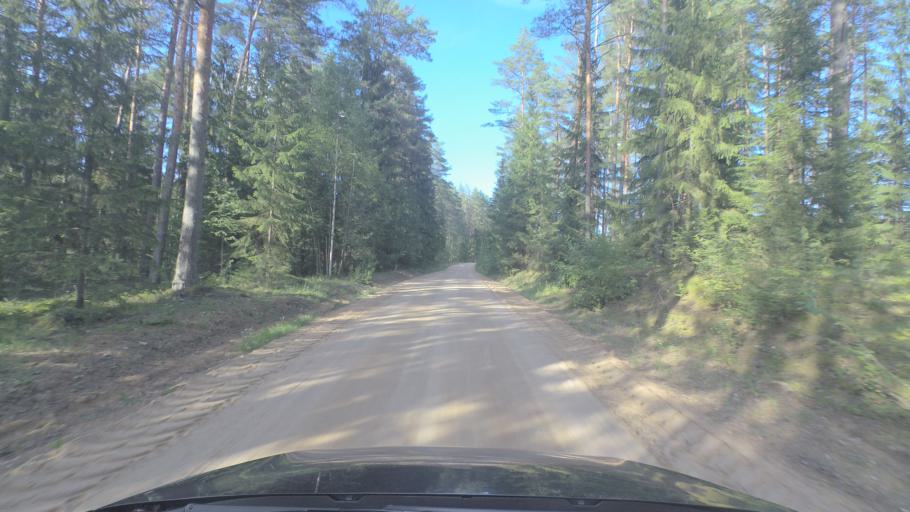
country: LT
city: Svencioneliai
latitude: 55.1642
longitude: 25.8295
